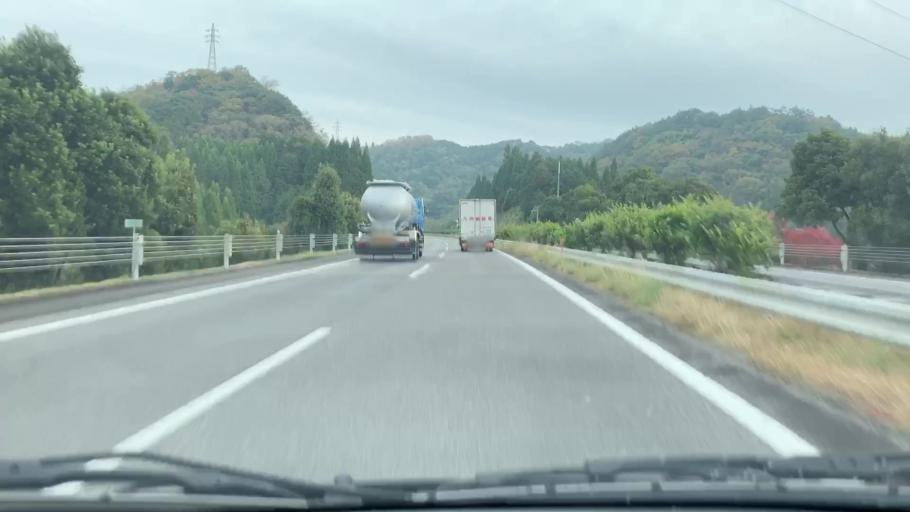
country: JP
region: Saga Prefecture
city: Takeocho-takeo
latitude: 33.2362
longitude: 130.0618
